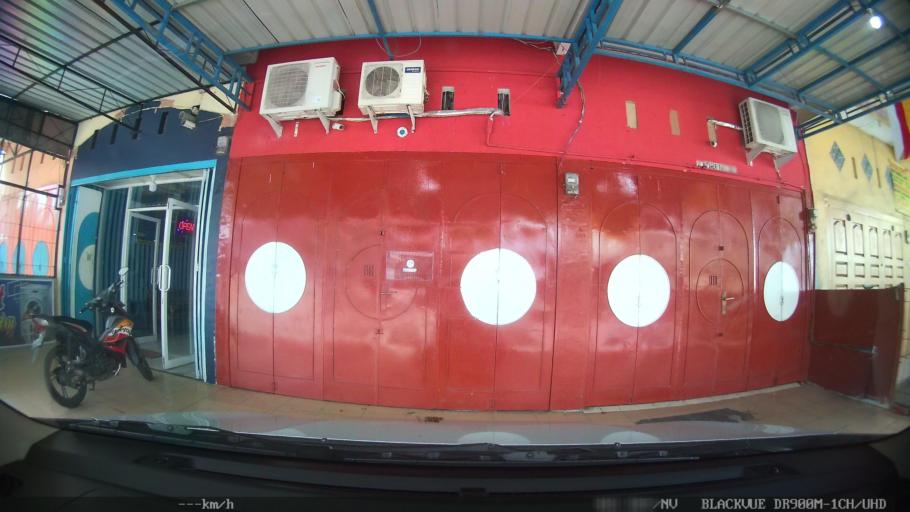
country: ID
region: North Sumatra
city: Sunggal
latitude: 3.6090
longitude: 98.6295
